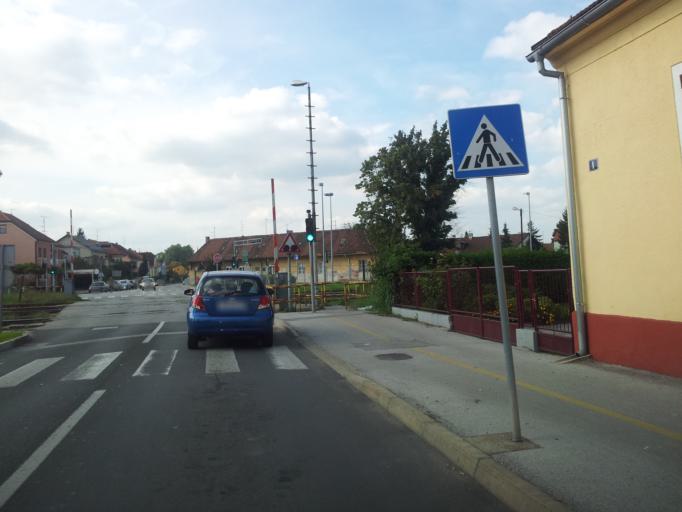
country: HR
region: Varazdinska
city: Varazdin
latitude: 46.3020
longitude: 16.3445
